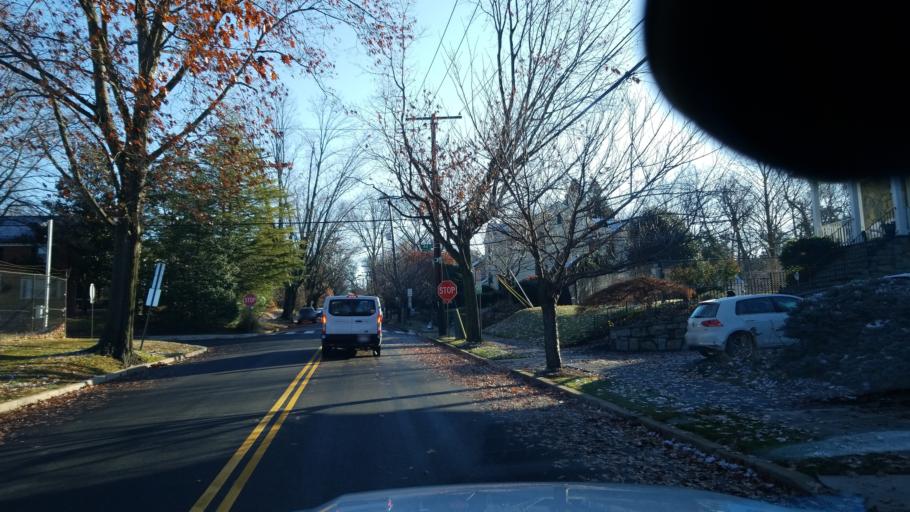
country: US
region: Maryland
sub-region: Montgomery County
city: Friendship Village
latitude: 38.9432
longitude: -77.0868
